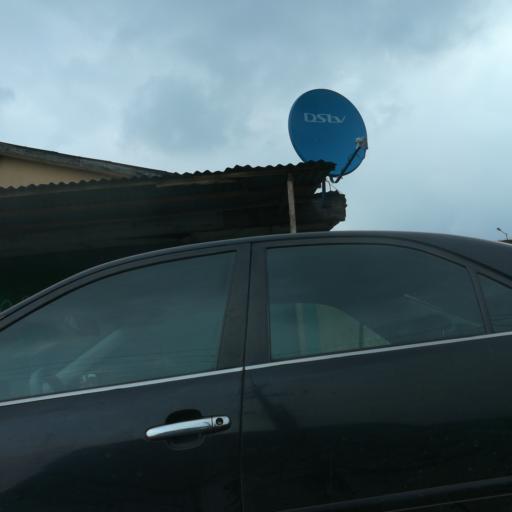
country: NG
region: Lagos
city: Agege
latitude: 6.5987
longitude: 3.2950
